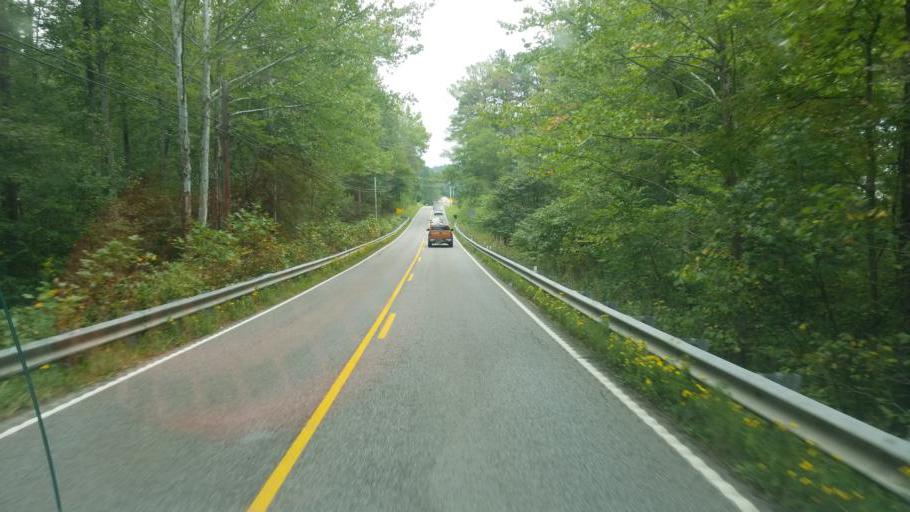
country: US
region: Kentucky
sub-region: Rowan County
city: Morehead
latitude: 38.2260
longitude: -83.4656
